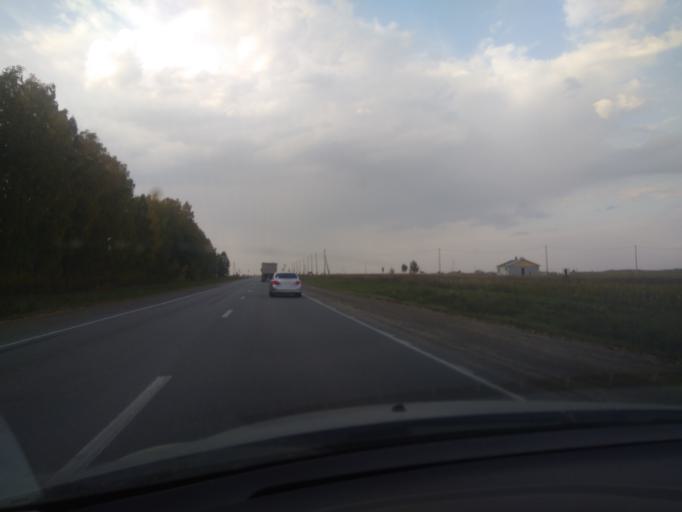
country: RU
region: Sverdlovsk
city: Sovkhoznyy
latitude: 56.6067
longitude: 61.3011
